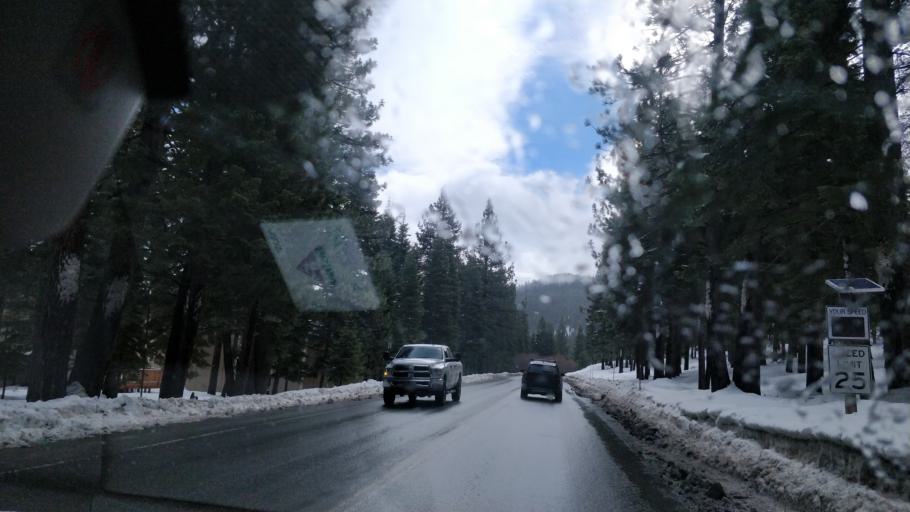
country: US
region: California
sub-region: Nevada County
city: Truckee
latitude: 39.2820
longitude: -120.1237
